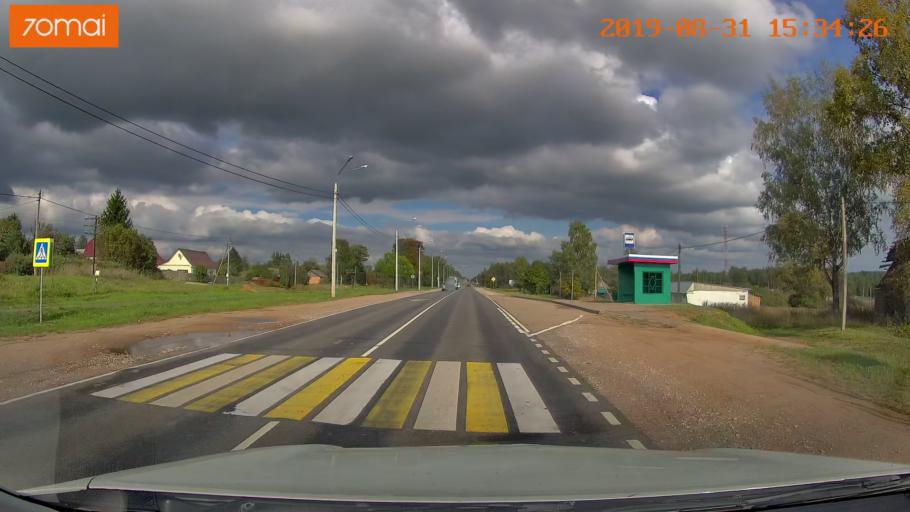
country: RU
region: Kaluga
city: Mosal'sk
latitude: 54.6005
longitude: 34.7200
